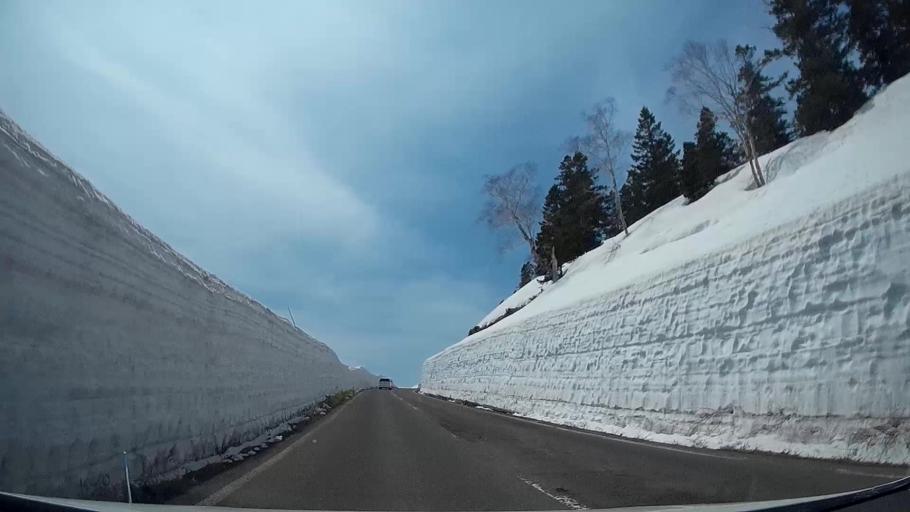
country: JP
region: Akita
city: Hanawa
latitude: 39.9546
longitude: 140.8845
